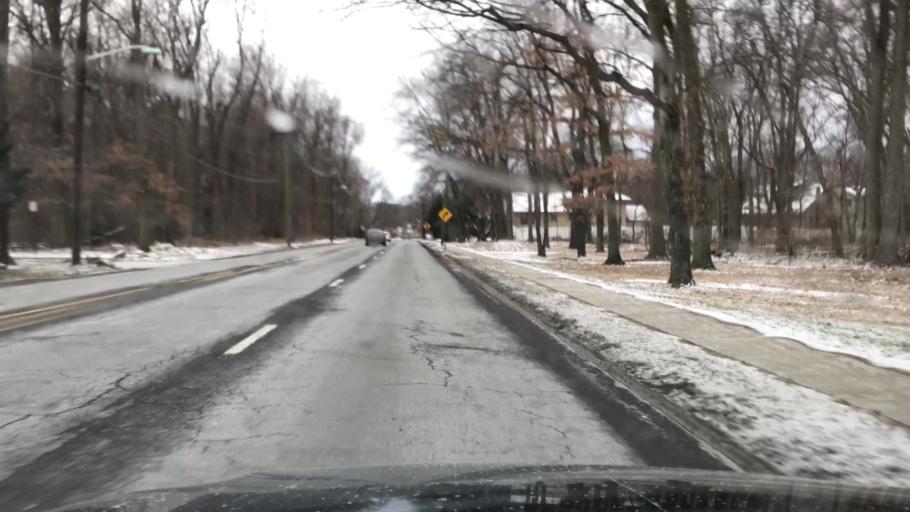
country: US
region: New Jersey
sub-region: Bergen County
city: Teaneck
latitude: 40.9152
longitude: -74.0207
